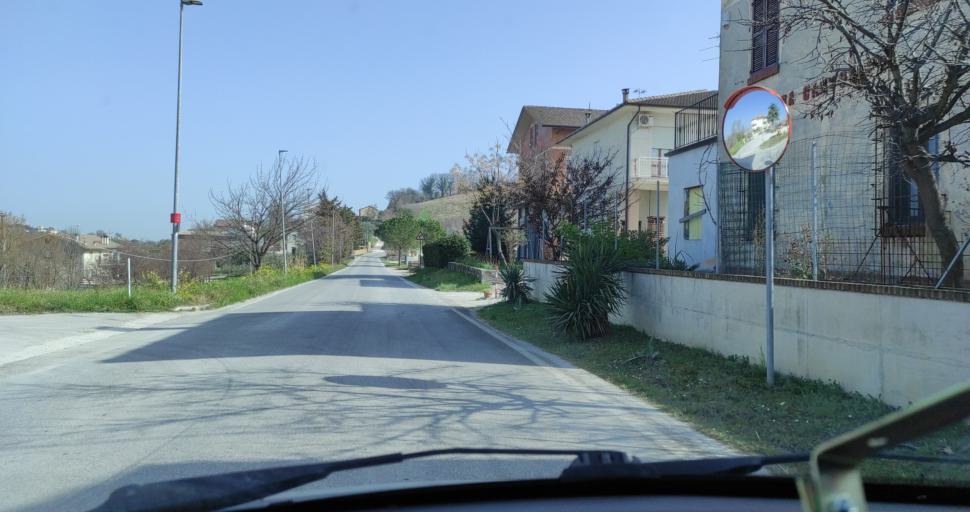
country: IT
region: The Marches
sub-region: Provincia di Macerata
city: Mogliano
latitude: 43.1830
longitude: 13.4586
